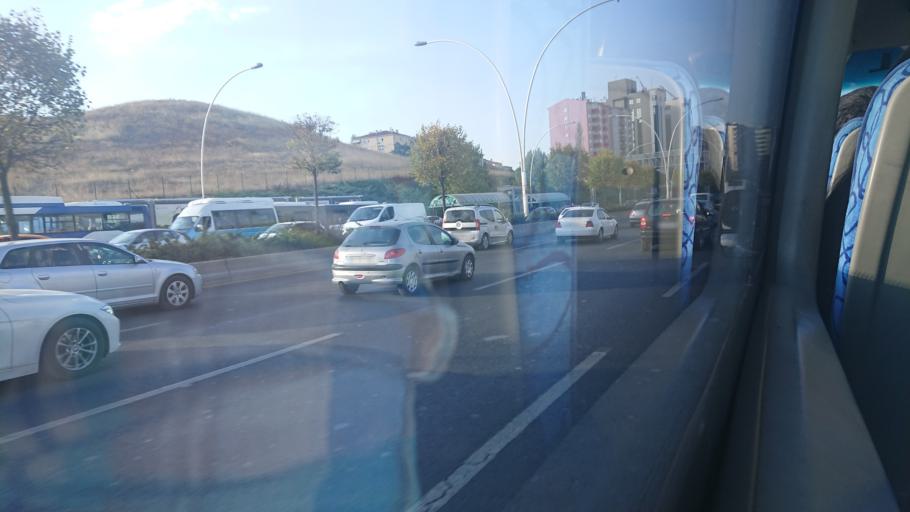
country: TR
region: Ankara
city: Ankara
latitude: 39.9225
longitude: 32.8144
